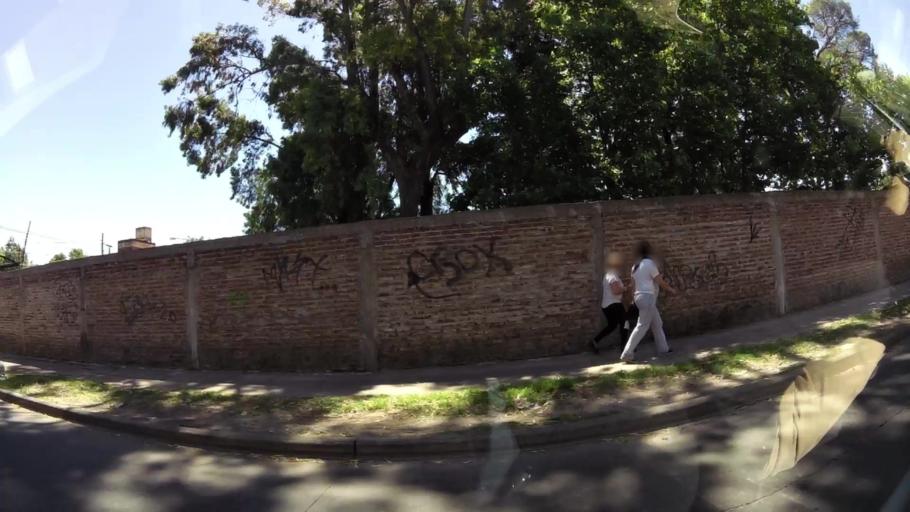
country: AR
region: Buenos Aires
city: Caseros
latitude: -34.5804
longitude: -58.5596
